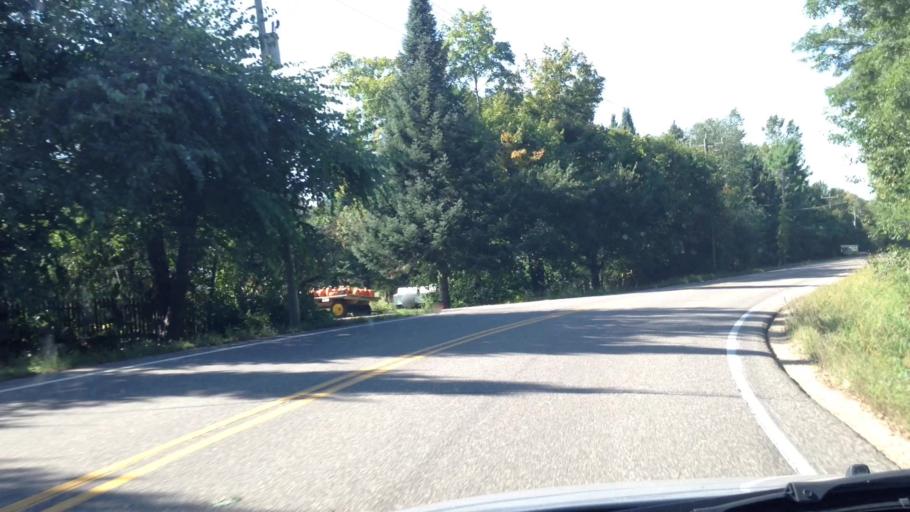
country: US
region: Minnesota
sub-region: Washington County
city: Stillwater
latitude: 45.0812
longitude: -92.8103
